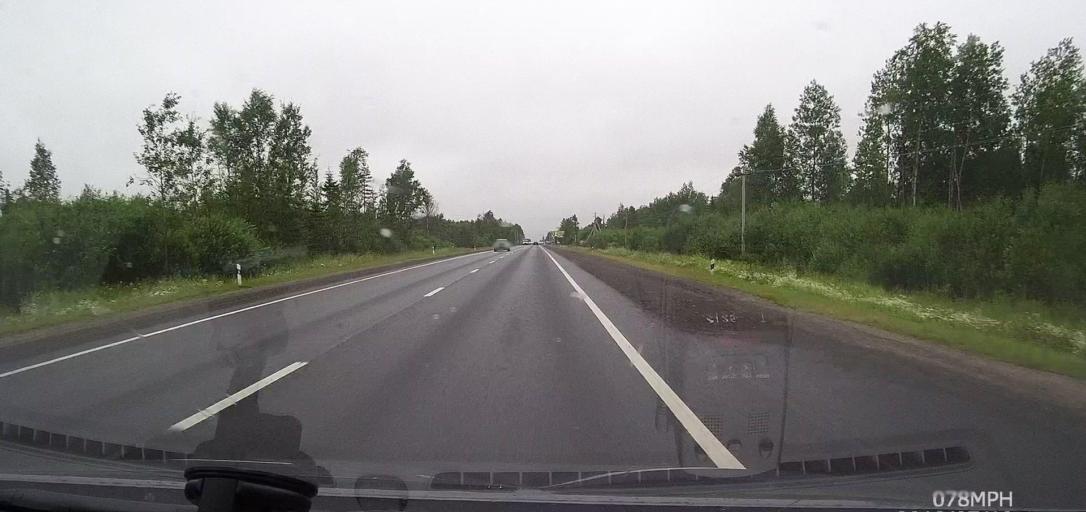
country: RU
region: Leningrad
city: Staraya Ladoga
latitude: 60.0021
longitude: 32.1190
